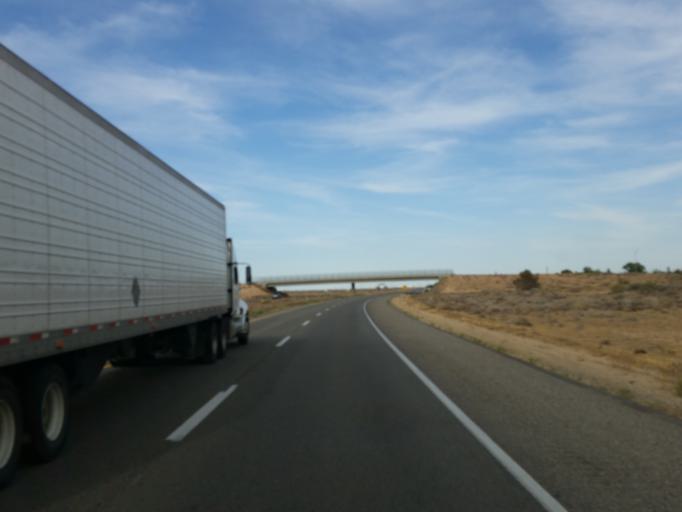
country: US
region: California
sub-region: Kern County
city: Boron
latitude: 35.0100
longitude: -117.6533
